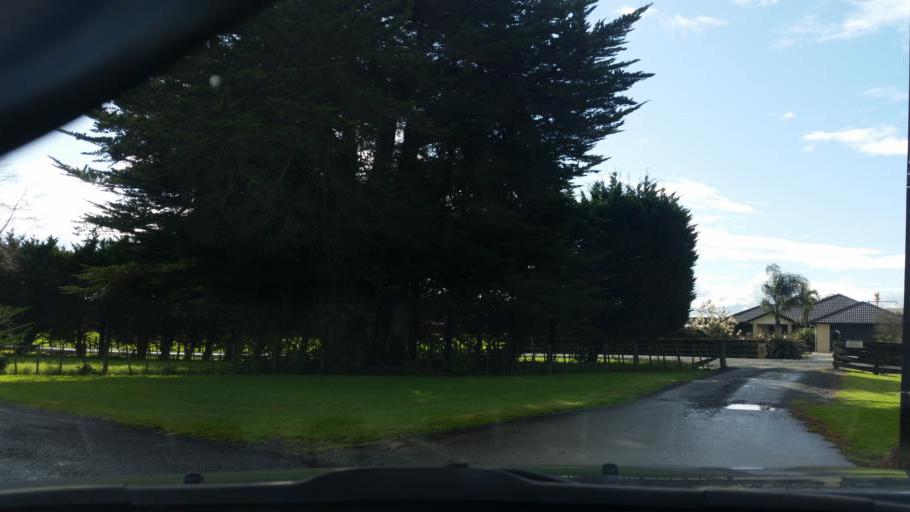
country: NZ
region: Northland
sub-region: Kaipara District
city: Dargaville
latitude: -35.9316
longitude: 173.8820
